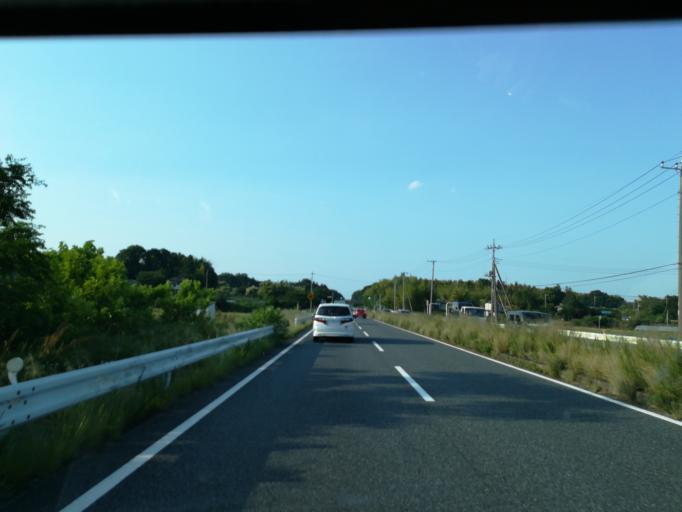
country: JP
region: Saitama
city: Kumagaya
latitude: 36.0987
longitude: 139.3647
